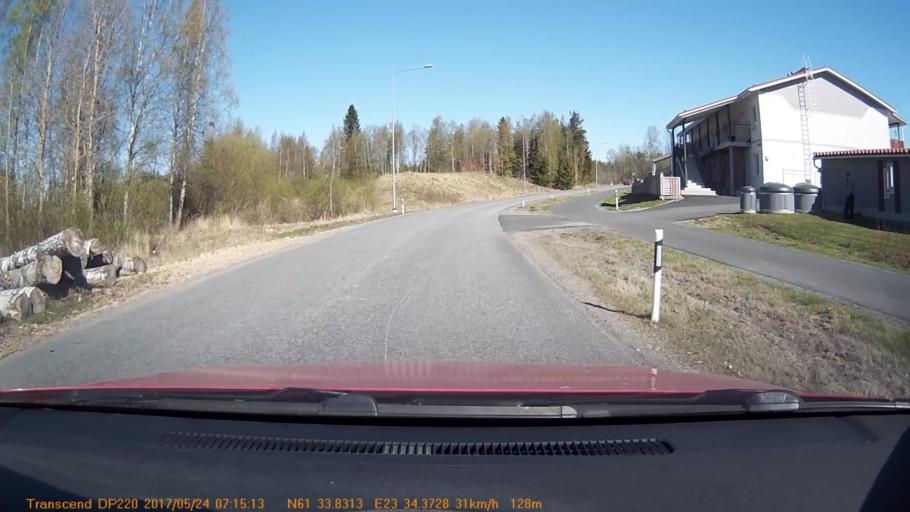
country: FI
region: Pirkanmaa
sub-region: Tampere
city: Yloejaervi
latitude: 61.5638
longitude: 23.5729
